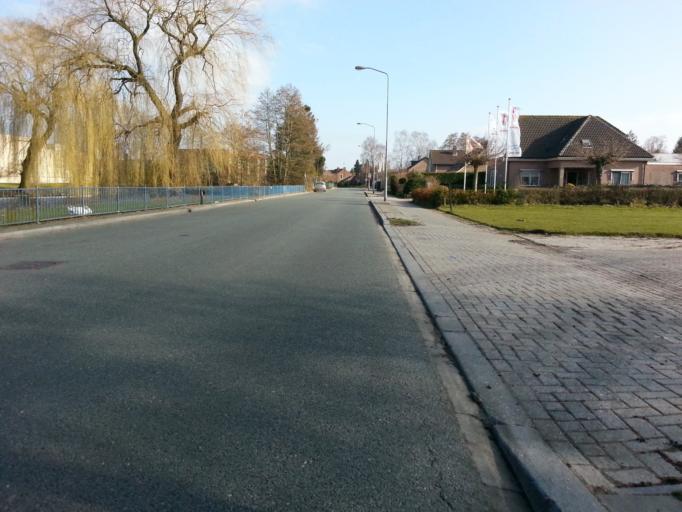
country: NL
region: Utrecht
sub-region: Gemeente Utrechtse Heuvelrug
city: Overberg
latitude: 52.0825
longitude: 5.4714
